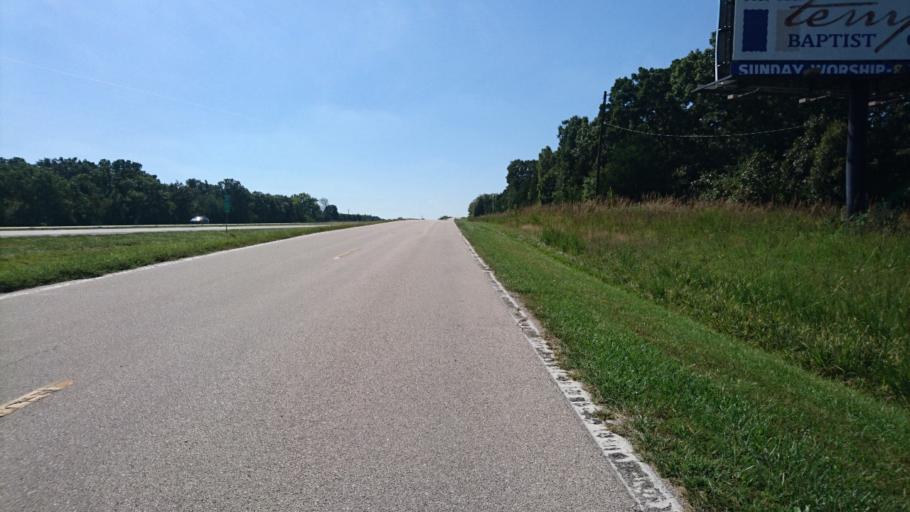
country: US
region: Missouri
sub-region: Franklin County
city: Sullivan
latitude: 38.2643
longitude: -91.1140
